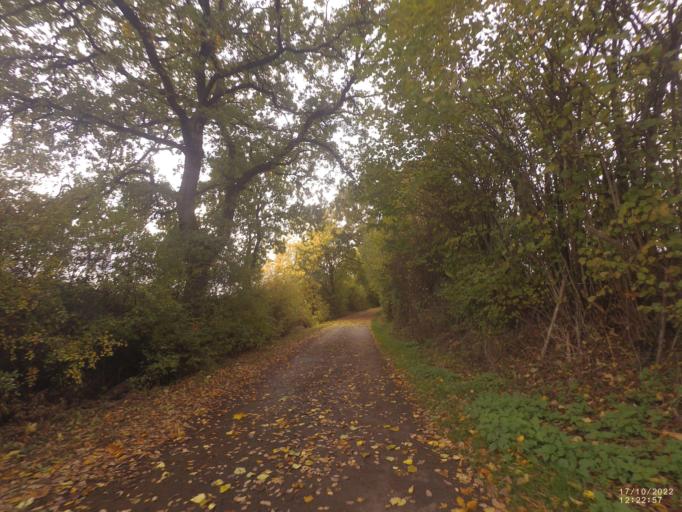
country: DE
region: Rheinland-Pfalz
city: Schonbach
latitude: 50.2154
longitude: 6.9531
